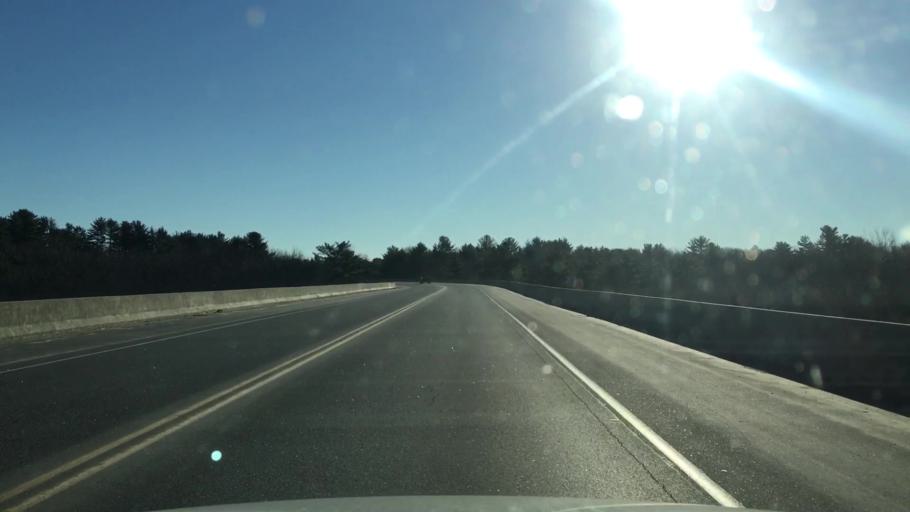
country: US
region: Maine
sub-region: Kennebec County
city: Waterville
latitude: 44.5303
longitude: -69.6461
